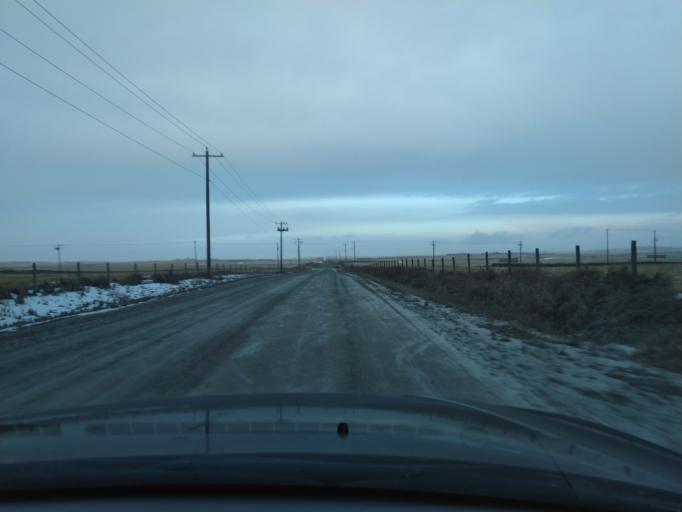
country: CA
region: Alberta
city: Airdrie
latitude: 51.1815
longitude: -114.0248
